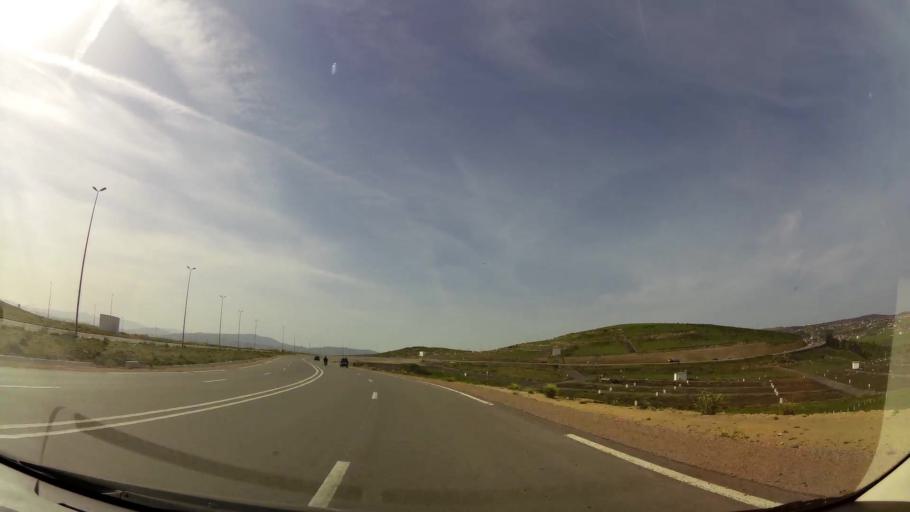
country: MA
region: Tanger-Tetouan
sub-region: Tanger-Assilah
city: Tangier
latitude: 35.7036
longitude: -5.8163
